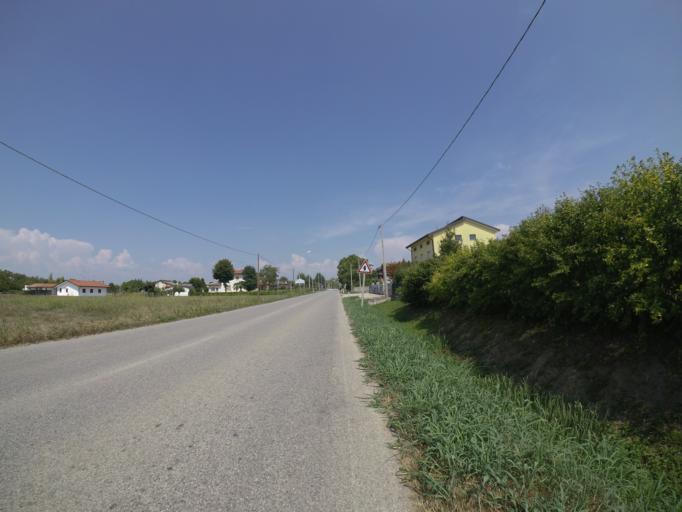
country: IT
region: Friuli Venezia Giulia
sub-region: Provincia di Udine
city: Pocenia
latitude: 45.8660
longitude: 13.1101
